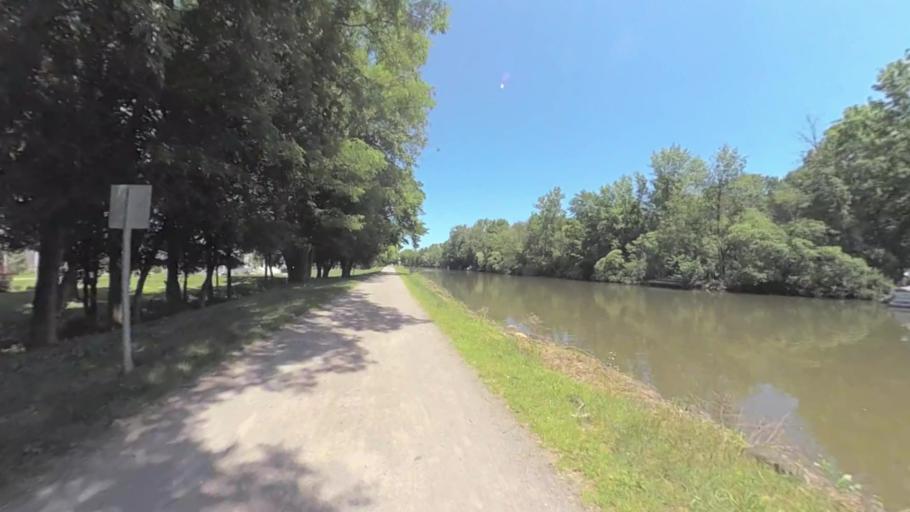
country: US
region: New York
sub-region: Monroe County
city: Fairport
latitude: 43.0945
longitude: -77.4558
